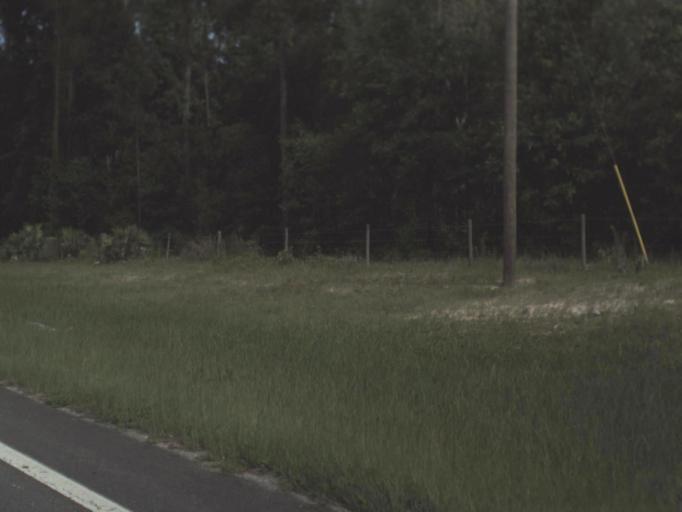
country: US
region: Florida
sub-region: Clay County
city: Green Cove Springs
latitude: 29.9833
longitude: -81.7493
